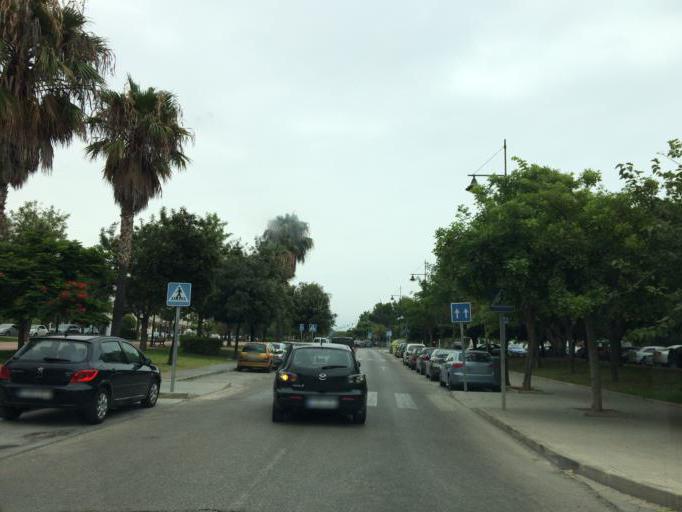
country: ES
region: Andalusia
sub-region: Provincia de Malaga
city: Torremolinos
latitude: 36.6355
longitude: -4.4901
